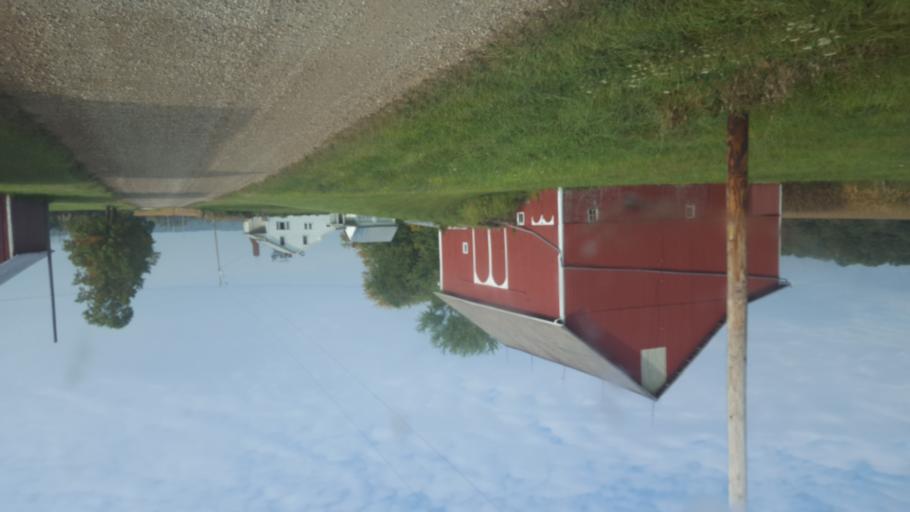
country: US
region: Ohio
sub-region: Knox County
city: Fredericktown
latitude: 40.4427
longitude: -82.6441
